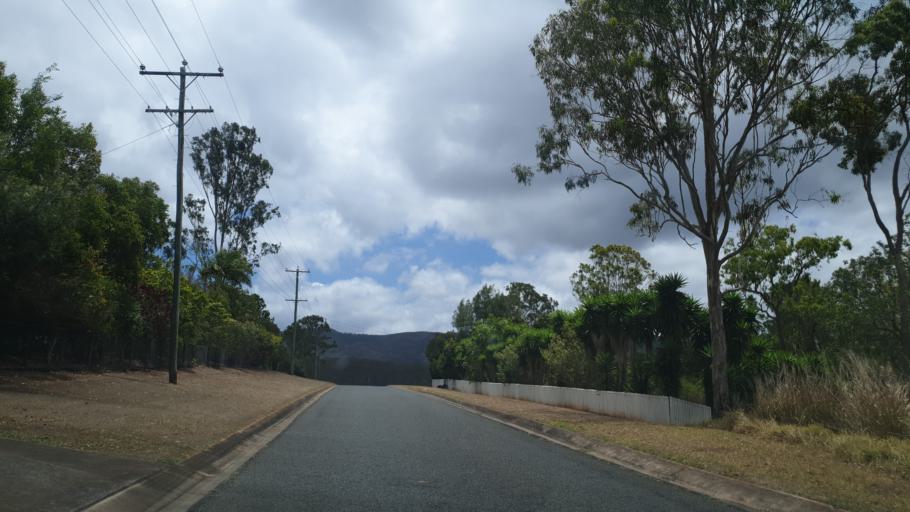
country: AU
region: Queensland
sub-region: Tablelands
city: Tolga
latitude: -17.2098
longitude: 145.4457
